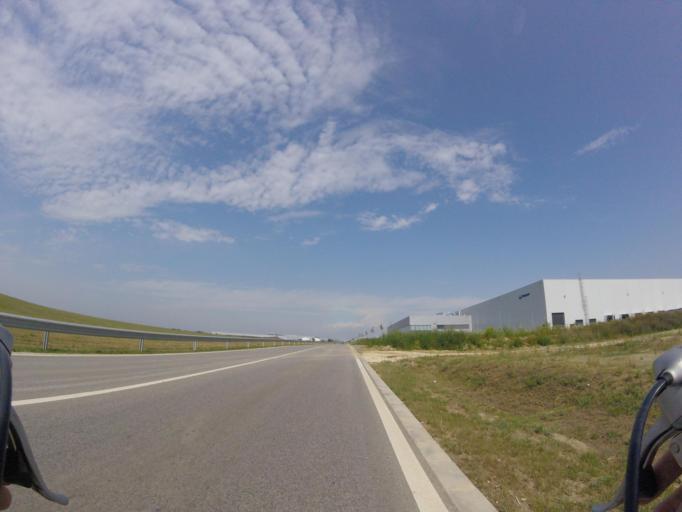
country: HU
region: Komarom-Esztergom
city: Tatabanya
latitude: 47.5792
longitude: 18.3519
